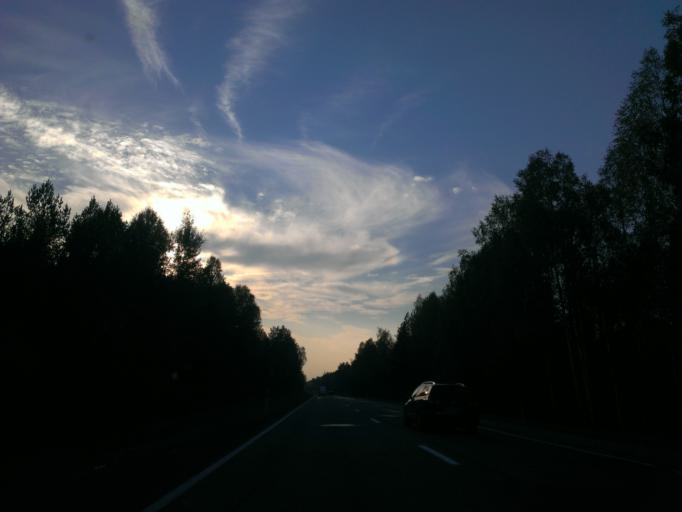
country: LV
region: Seja
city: Loja
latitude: 57.1087
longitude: 24.6093
